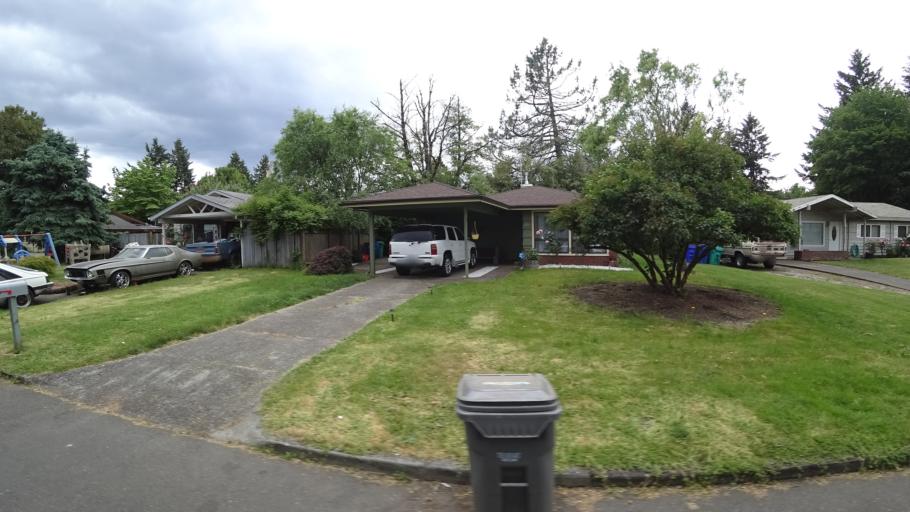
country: US
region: Oregon
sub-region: Clackamas County
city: Happy Valley
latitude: 45.5008
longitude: -122.5122
